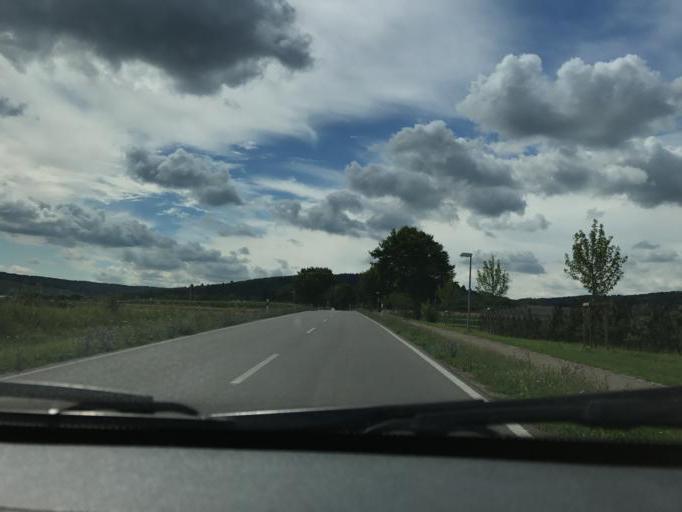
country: DE
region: Baden-Wuerttemberg
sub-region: Regierungsbezirk Stuttgart
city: Weinstadt-Endersbach
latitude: 48.7995
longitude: 9.3362
